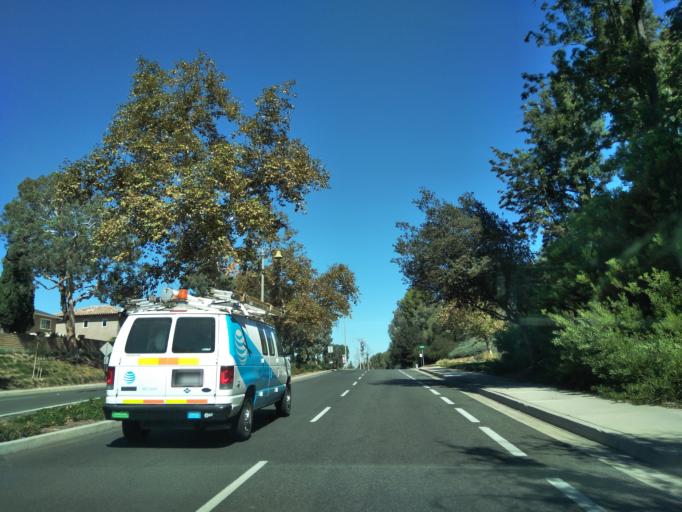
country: US
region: California
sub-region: Orange County
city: Mission Viejo
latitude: 33.6232
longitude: -117.6606
